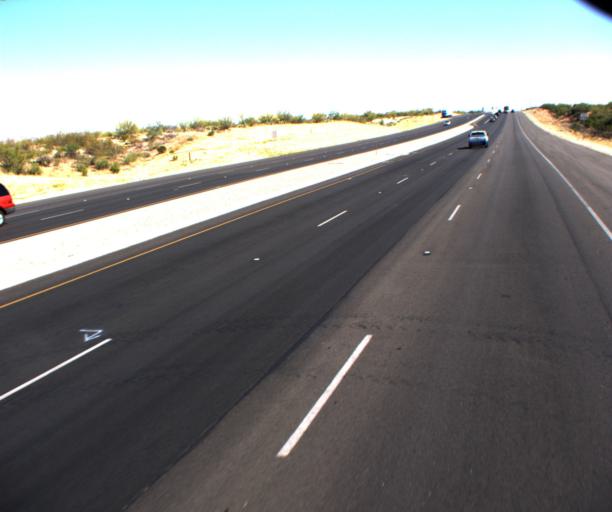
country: US
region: Arizona
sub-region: Pima County
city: Oro Valley
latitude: 32.4317
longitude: -110.9339
